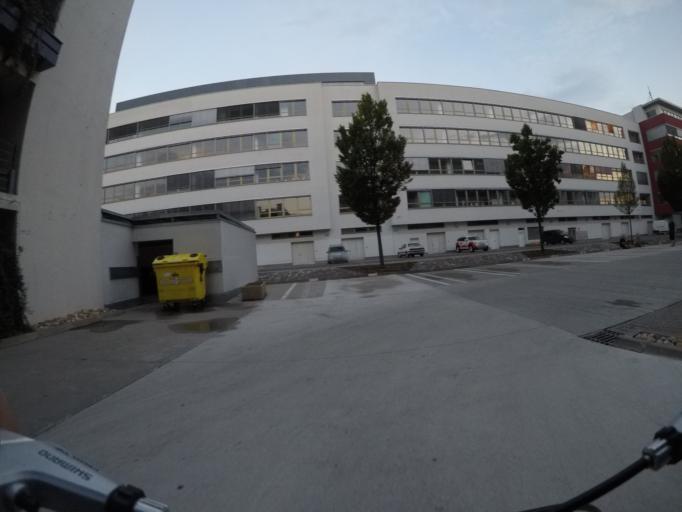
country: SK
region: Bratislavsky
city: Bratislava
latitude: 48.1650
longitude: 17.1771
